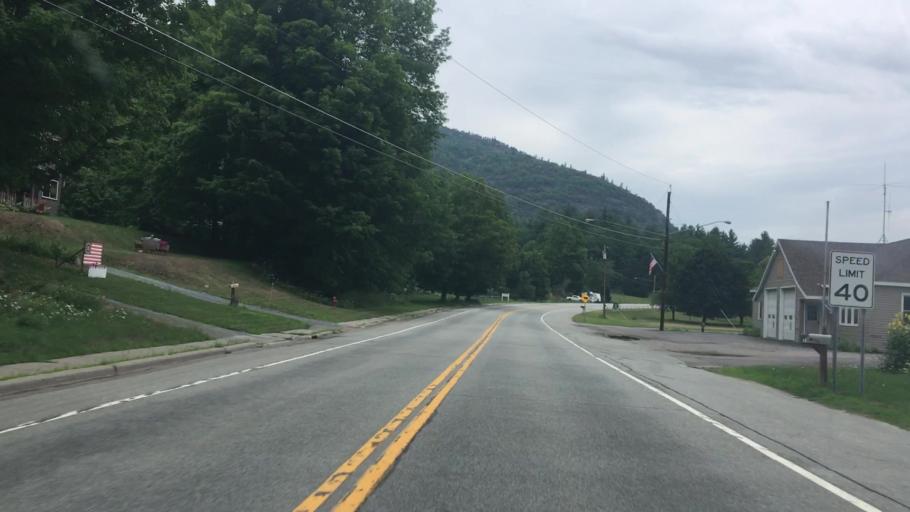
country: US
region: New York
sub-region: Essex County
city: Lake Placid
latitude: 44.3384
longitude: -73.7737
